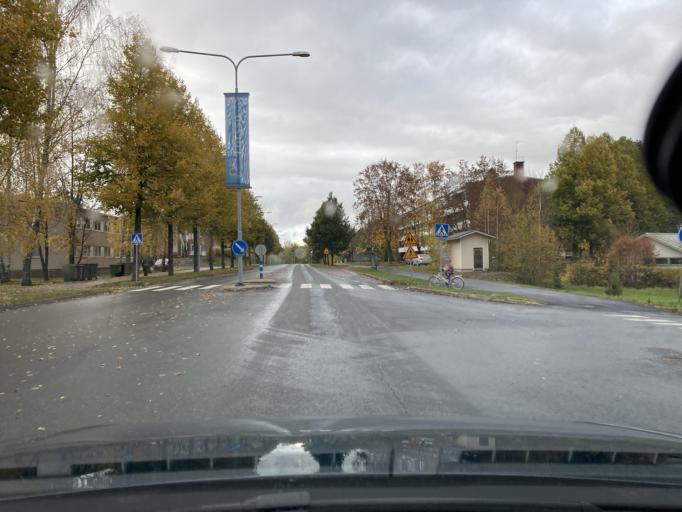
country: FI
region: Haeme
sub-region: Forssa
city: Forssa
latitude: 60.8199
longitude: 23.6086
